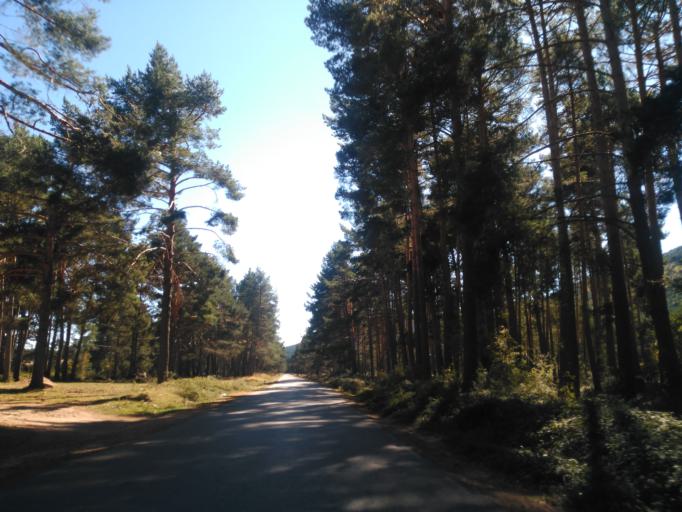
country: ES
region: Castille and Leon
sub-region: Provincia de Soria
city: Vinuesa
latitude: 41.9397
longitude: -2.7792
